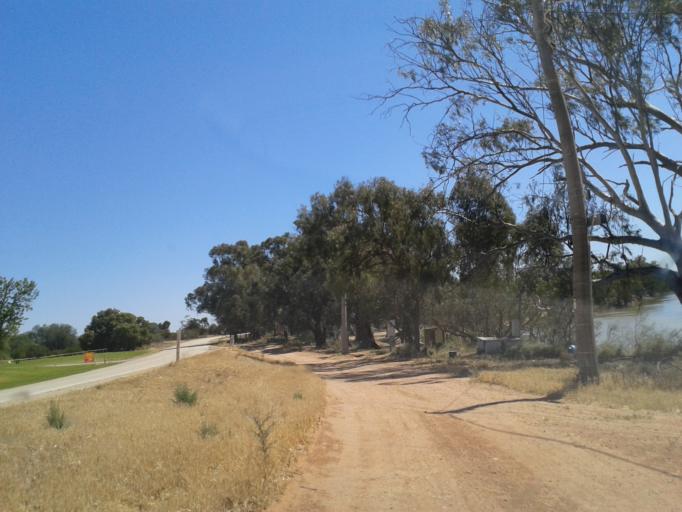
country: AU
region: Victoria
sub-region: Swan Hill
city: Swan Hill
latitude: -34.7150
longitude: 143.1481
